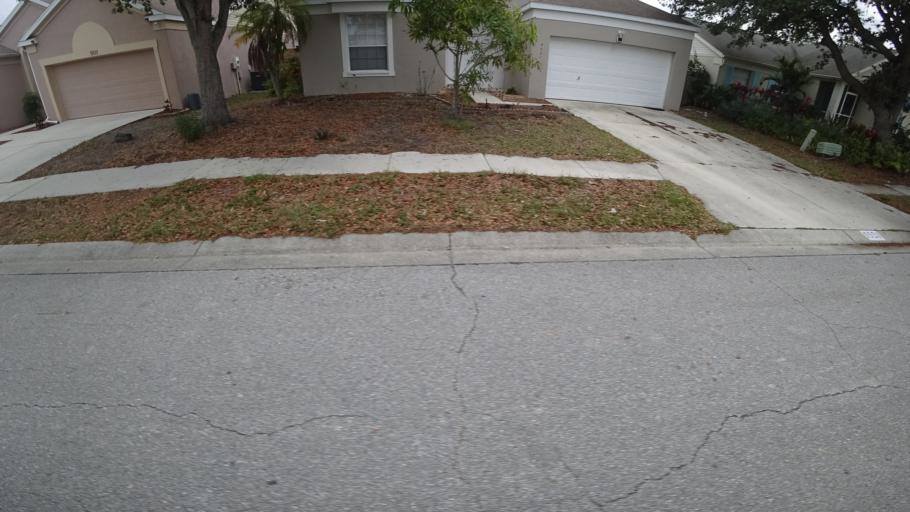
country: US
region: Florida
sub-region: Manatee County
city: Samoset
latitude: 27.4414
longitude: -82.5018
